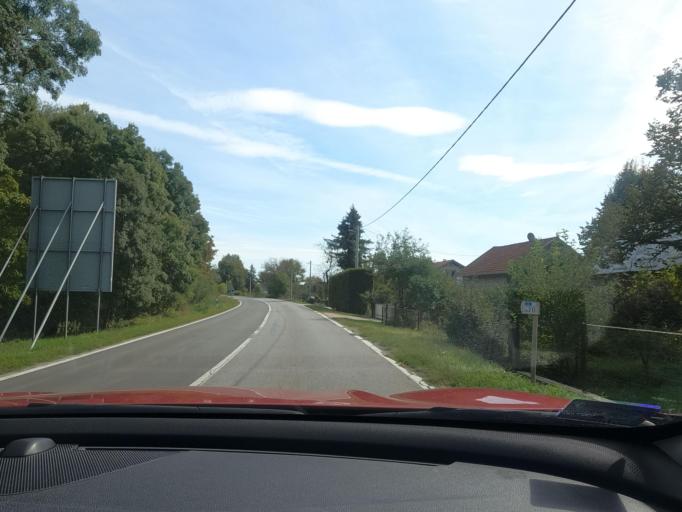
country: HR
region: Sisacko-Moslavacka
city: Budasevo
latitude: 45.4851
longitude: 16.4703
